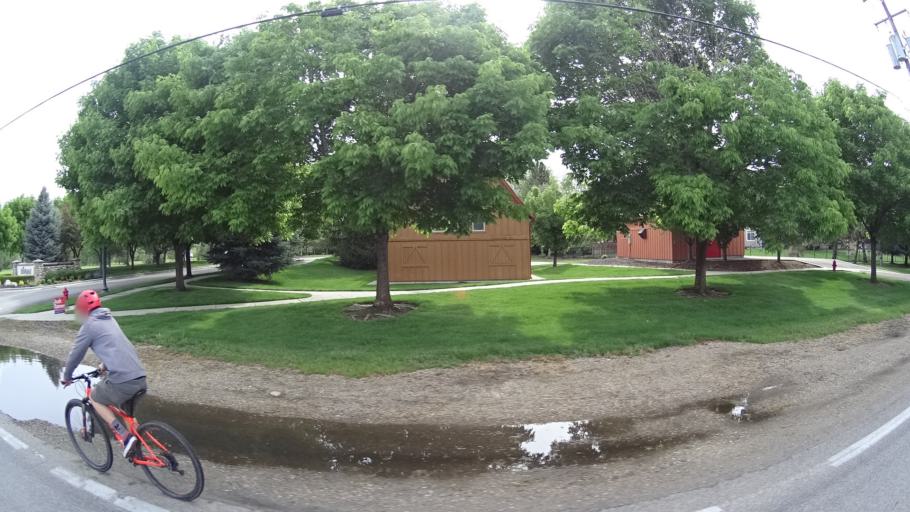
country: US
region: Idaho
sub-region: Ada County
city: Eagle
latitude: 43.7079
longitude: -116.3539
